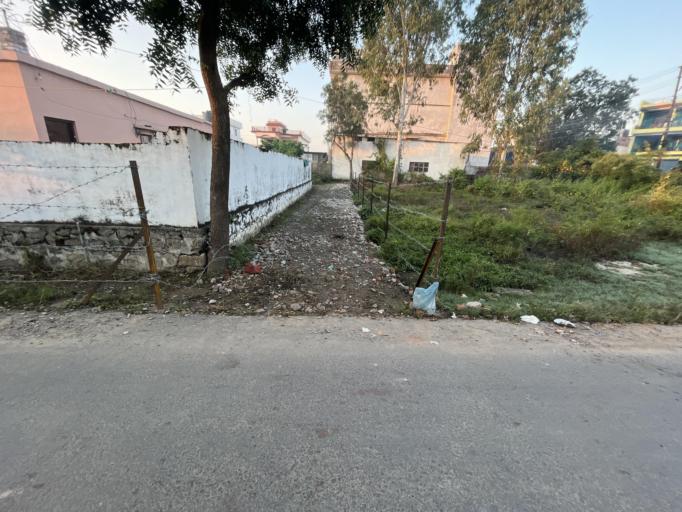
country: IN
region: Uttarakhand
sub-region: Naini Tal
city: Haldwani
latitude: 29.2082
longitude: 79.4951
